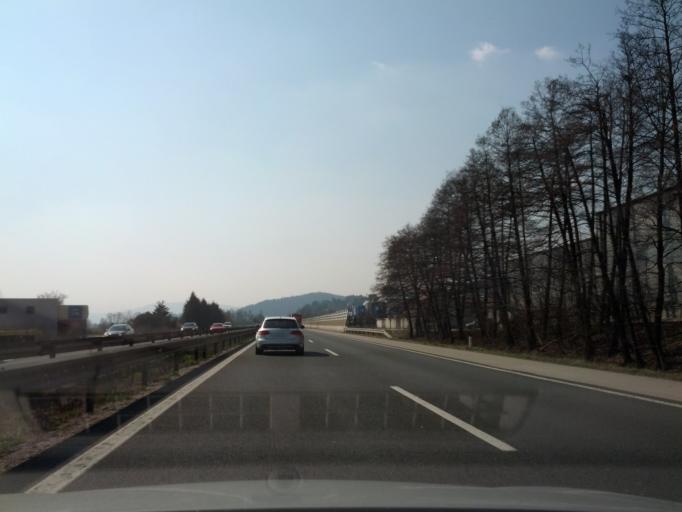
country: SI
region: Brezovica
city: Vnanje Gorice
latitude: 46.0225
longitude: 14.4171
